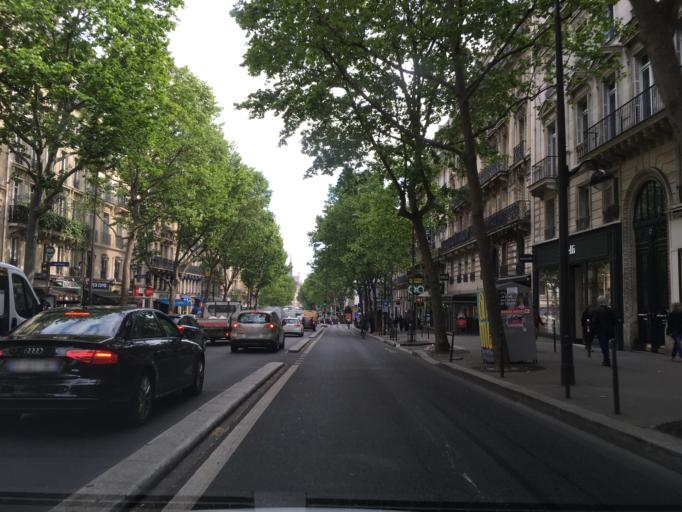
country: FR
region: Ile-de-France
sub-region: Paris
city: Paris
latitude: 48.8493
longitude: 2.3421
